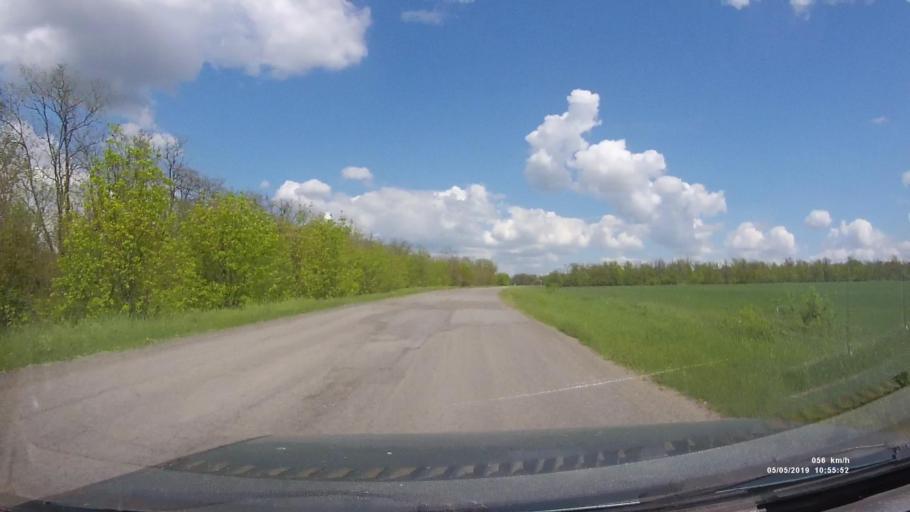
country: RU
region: Rostov
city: Ust'-Donetskiy
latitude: 47.6692
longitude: 40.8202
